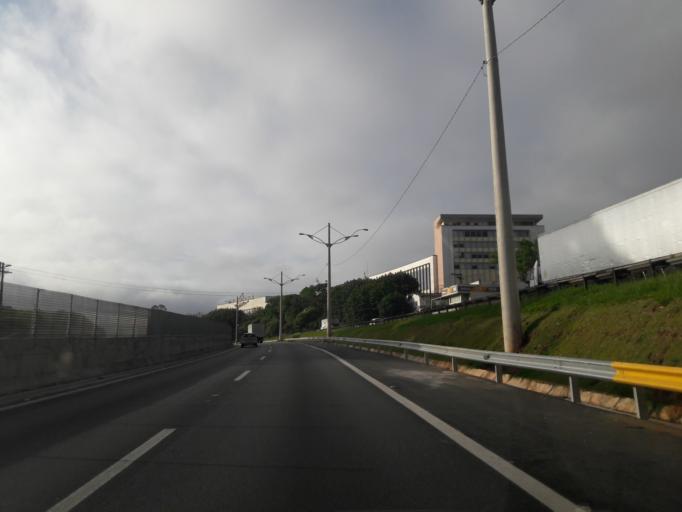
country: BR
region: Sao Paulo
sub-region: Sao Bernardo Do Campo
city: Sao Bernardo do Campo
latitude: -23.7132
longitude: -46.5614
